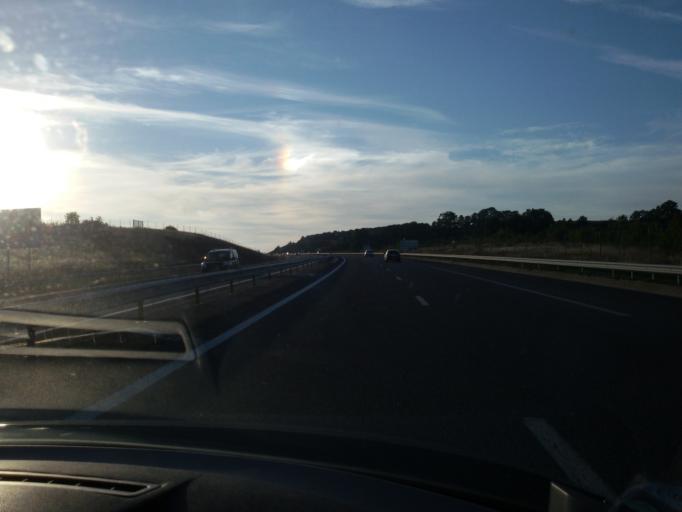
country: FR
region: Midi-Pyrenees
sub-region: Departement de l'Aveyron
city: La Cavalerie
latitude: 43.9970
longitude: 3.1686
